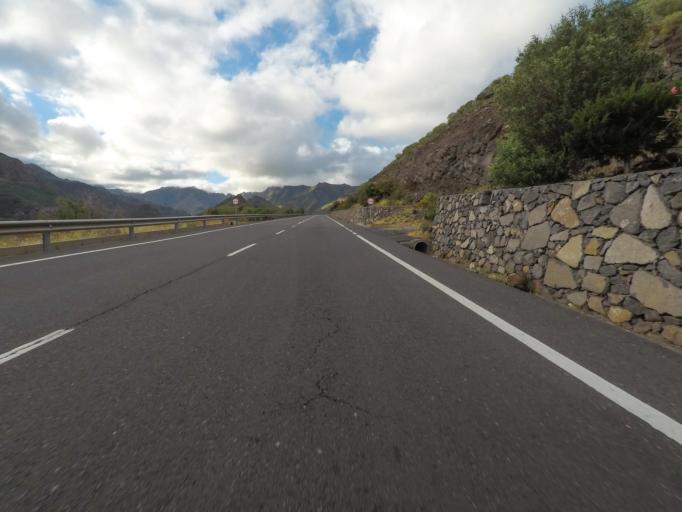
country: ES
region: Canary Islands
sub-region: Provincia de Santa Cruz de Tenerife
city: San Sebastian de la Gomera
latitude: 28.1021
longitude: -17.1212
